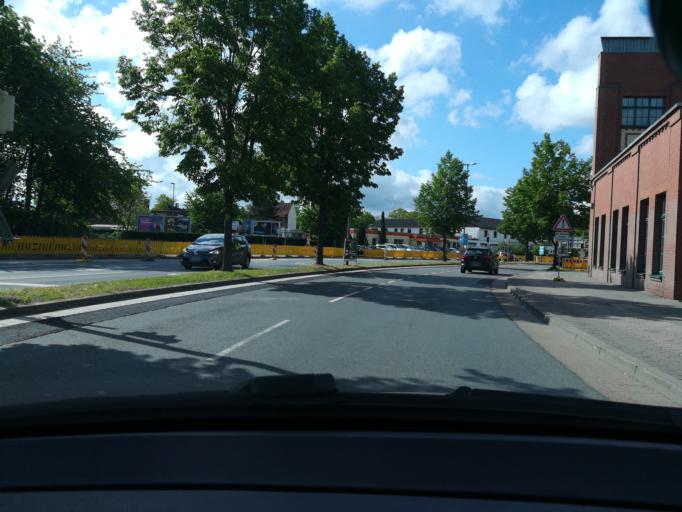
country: DE
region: North Rhine-Westphalia
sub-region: Regierungsbezirk Detmold
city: Minden
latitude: 52.2974
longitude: 8.9363
